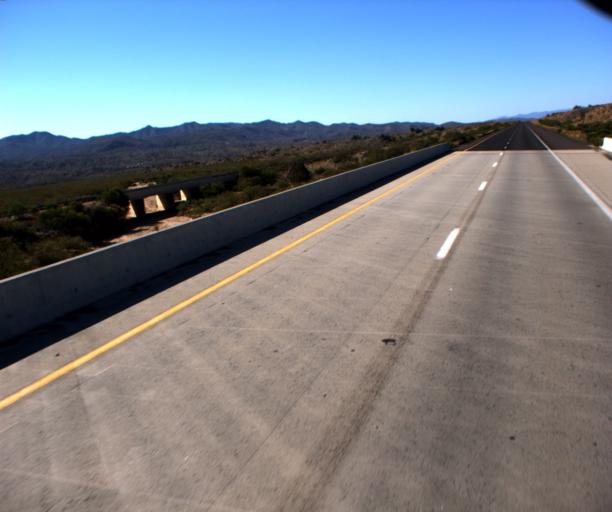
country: US
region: Arizona
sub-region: Mohave County
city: Kingman
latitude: 35.0782
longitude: -113.6660
